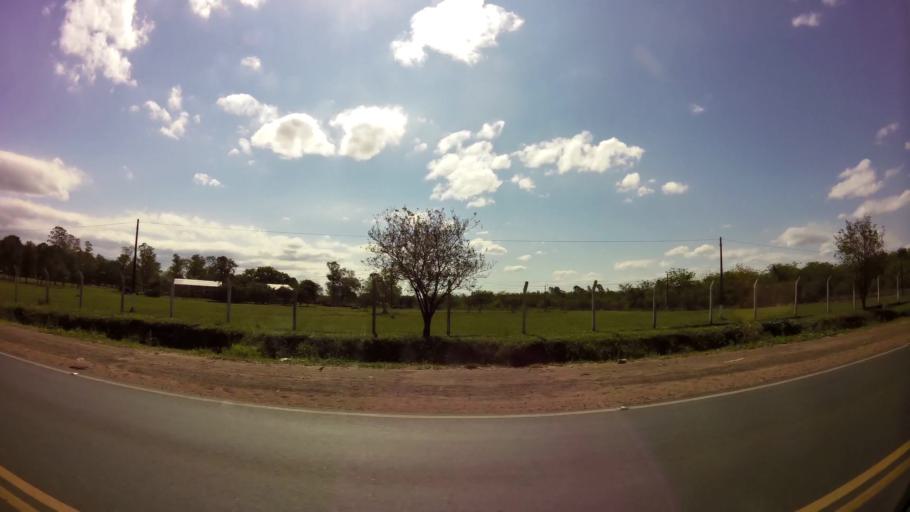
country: PY
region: Central
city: Fernando de la Mora
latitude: -25.2665
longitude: -57.5229
